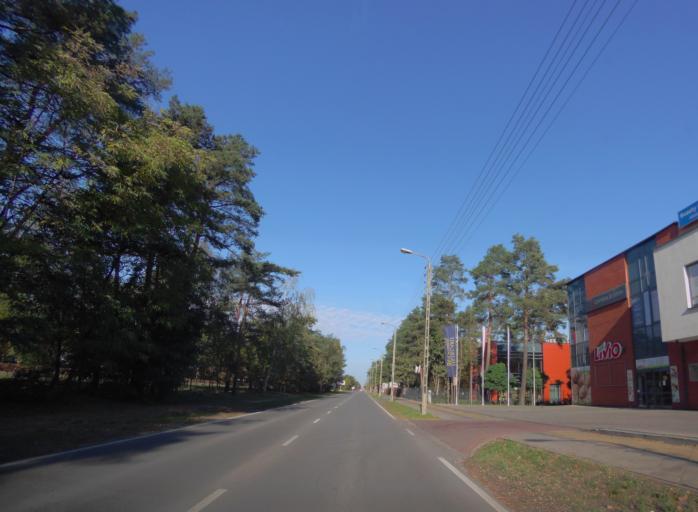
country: PL
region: Masovian Voivodeship
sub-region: Powiat otwocki
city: Jozefow
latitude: 52.1389
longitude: 21.2344
